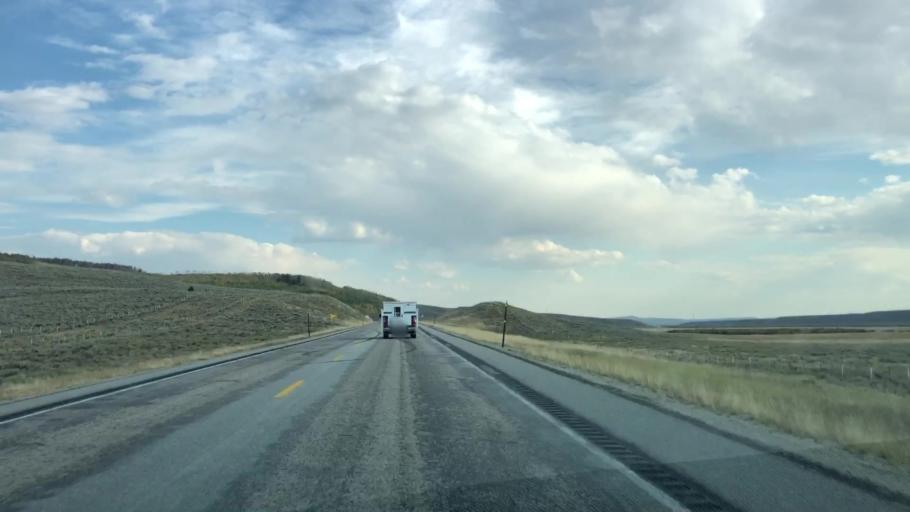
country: US
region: Wyoming
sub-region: Sublette County
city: Pinedale
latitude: 43.0947
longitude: -110.1666
